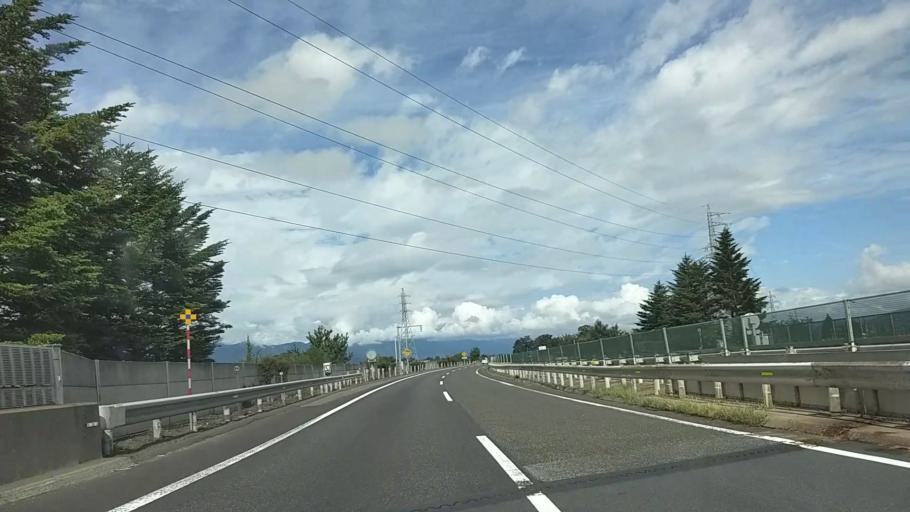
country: JP
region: Nagano
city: Matsumoto
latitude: 36.2035
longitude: 137.9316
